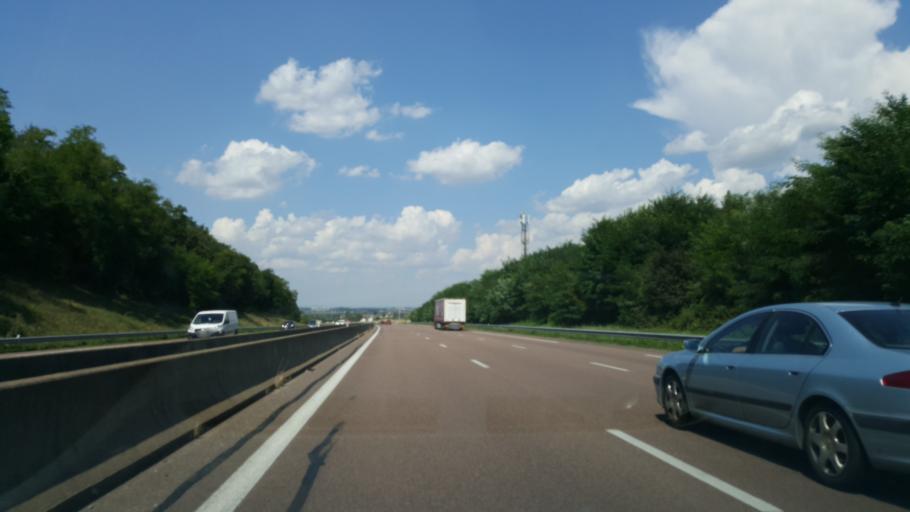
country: FR
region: Bourgogne
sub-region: Departement de Saone-et-Loire
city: Sennecey-le-Grand
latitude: 46.6433
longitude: 4.8597
